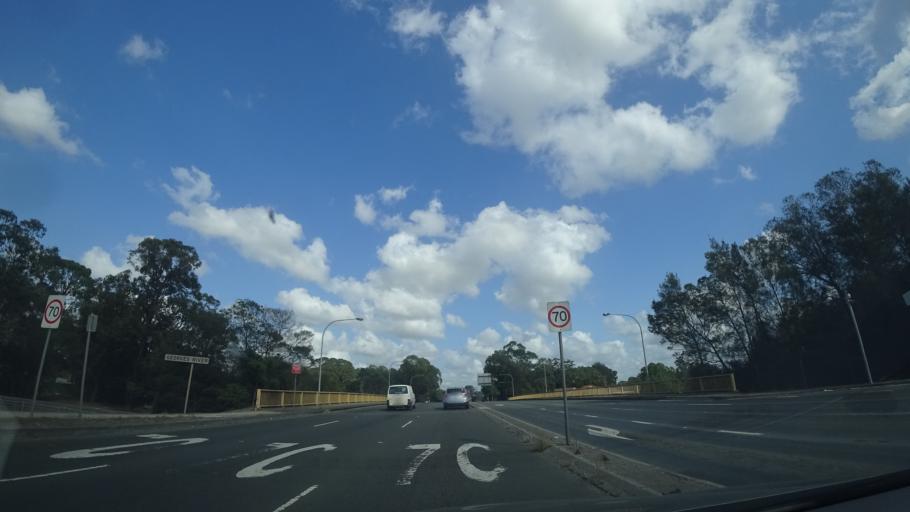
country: AU
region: New South Wales
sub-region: Bankstown
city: Milperra
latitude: -33.9290
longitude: 150.9801
